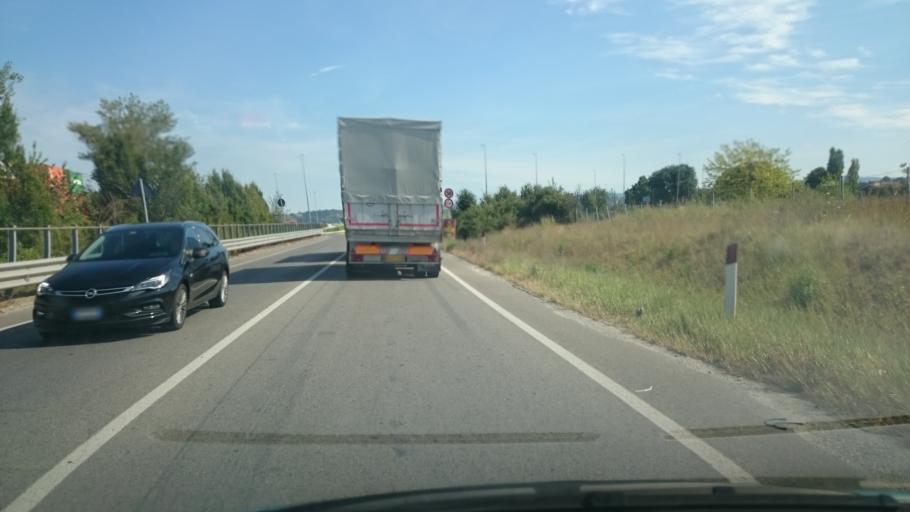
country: IT
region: Emilia-Romagna
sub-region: Provincia di Reggio Emilia
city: Veggia-Villalunga
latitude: 44.5665
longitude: 10.7556
